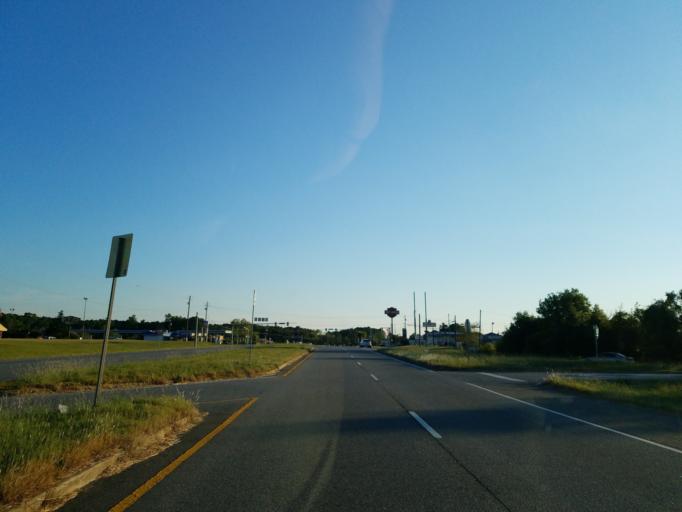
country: US
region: Georgia
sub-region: Bartow County
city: Cartersville
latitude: 34.2435
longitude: -84.7745
